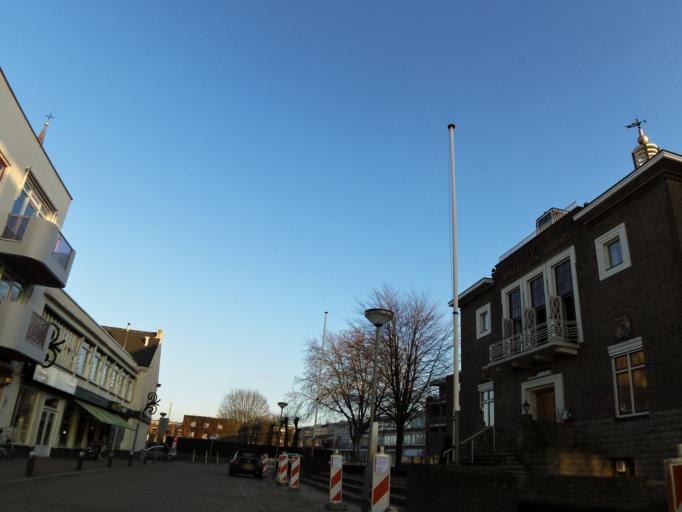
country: NL
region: Limburg
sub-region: Gemeente Kerkrade
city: Kerkrade
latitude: 50.9158
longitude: 6.0513
